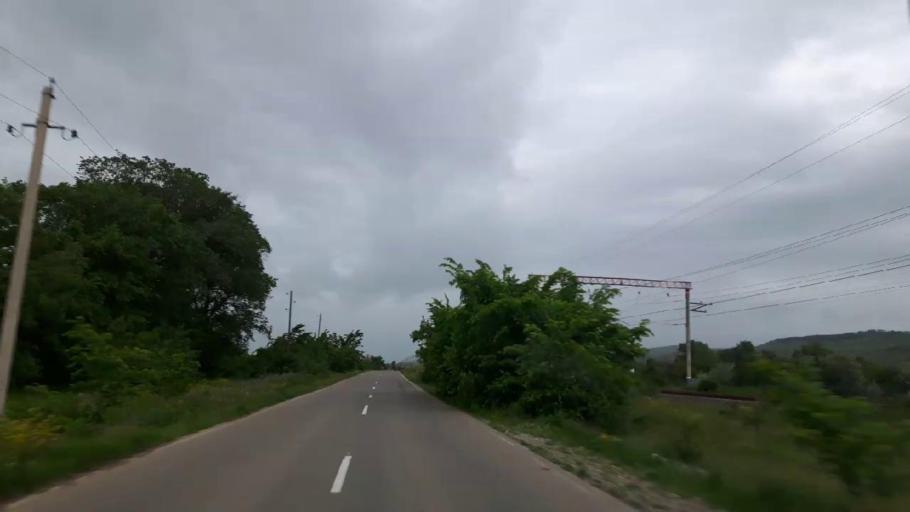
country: GE
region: Shida Kartli
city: Gori
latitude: 41.9951
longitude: 44.0256
